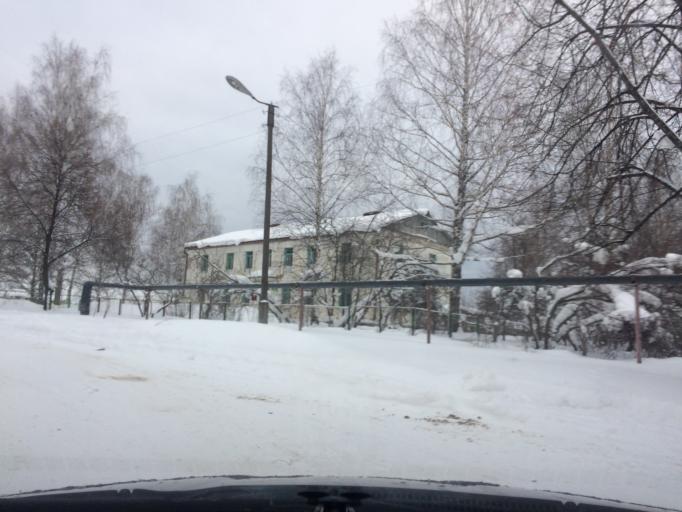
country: RU
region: Mariy-El
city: Mochalishche
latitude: 56.5441
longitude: 48.4063
